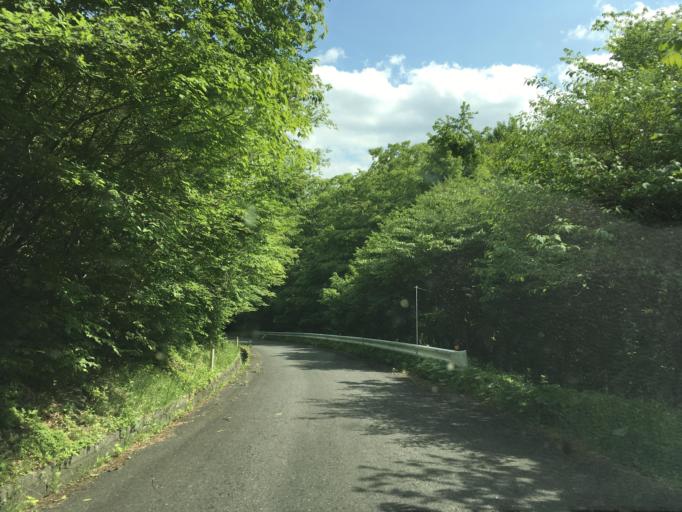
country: JP
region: Iwate
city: Ofunato
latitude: 38.9555
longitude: 141.4504
